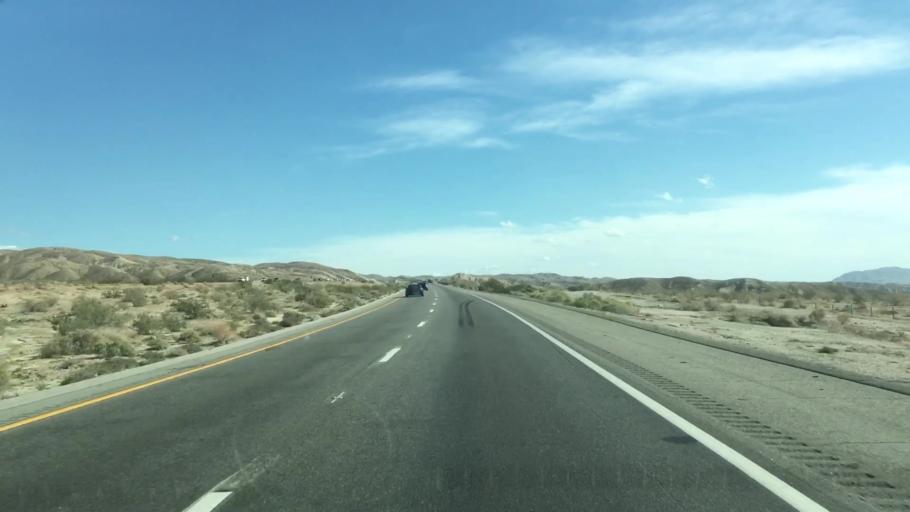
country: US
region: California
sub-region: Riverside County
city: Coachella
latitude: 33.7026
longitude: -116.1274
